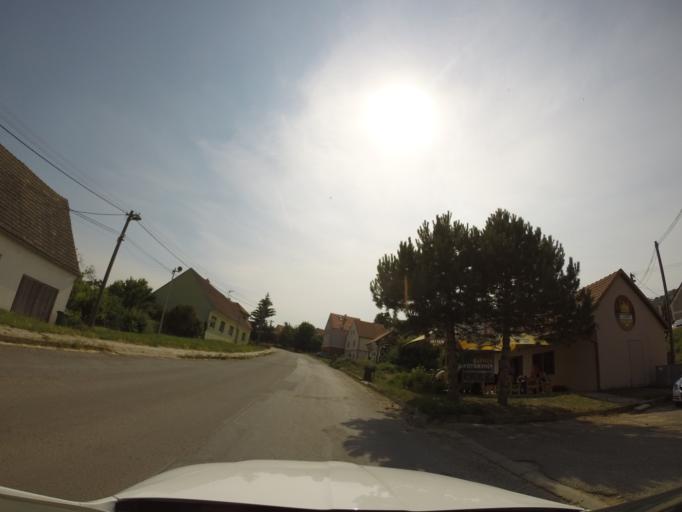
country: CZ
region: South Moravian
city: Sakvice
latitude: 48.8723
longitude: 16.6672
